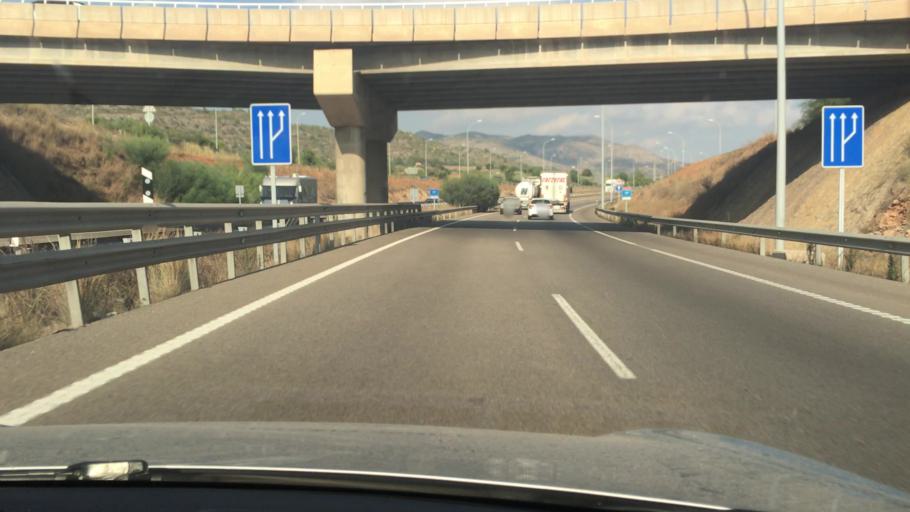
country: ES
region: Valencia
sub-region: Provincia de Castello
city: Borriol
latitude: 40.0073
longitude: -0.1139
